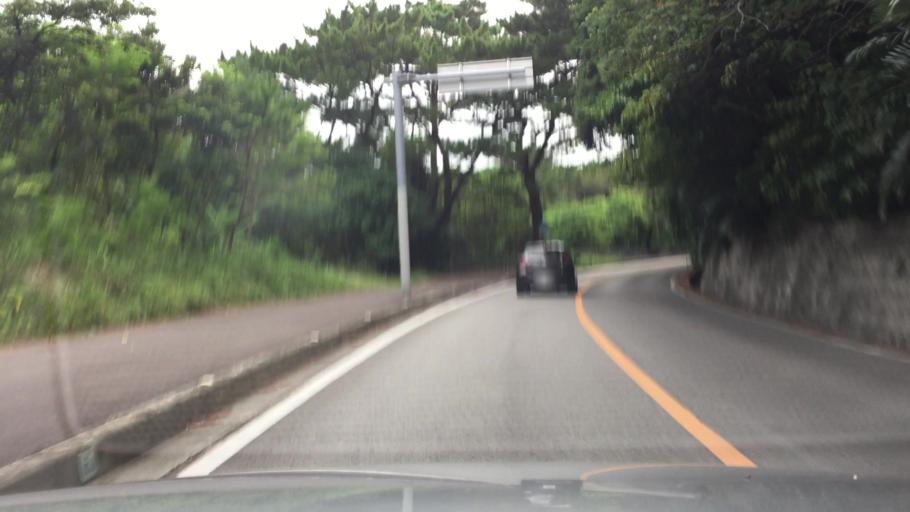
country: JP
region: Okinawa
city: Ishigaki
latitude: 24.4486
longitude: 124.1324
